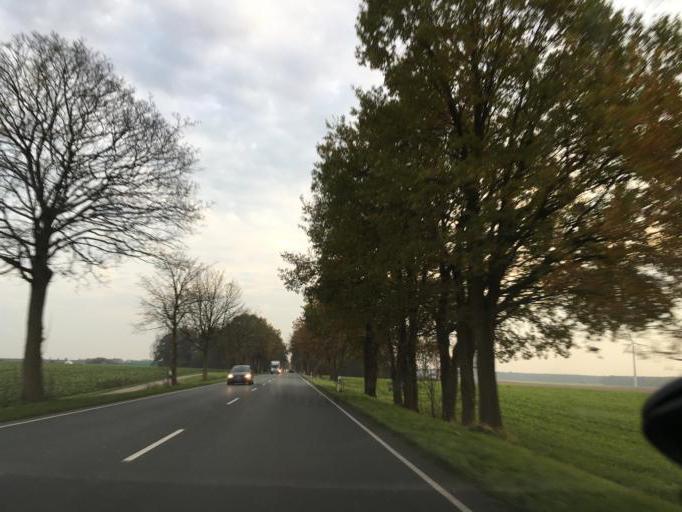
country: DE
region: Lower Saxony
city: Bergen
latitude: 52.7882
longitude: 9.9730
